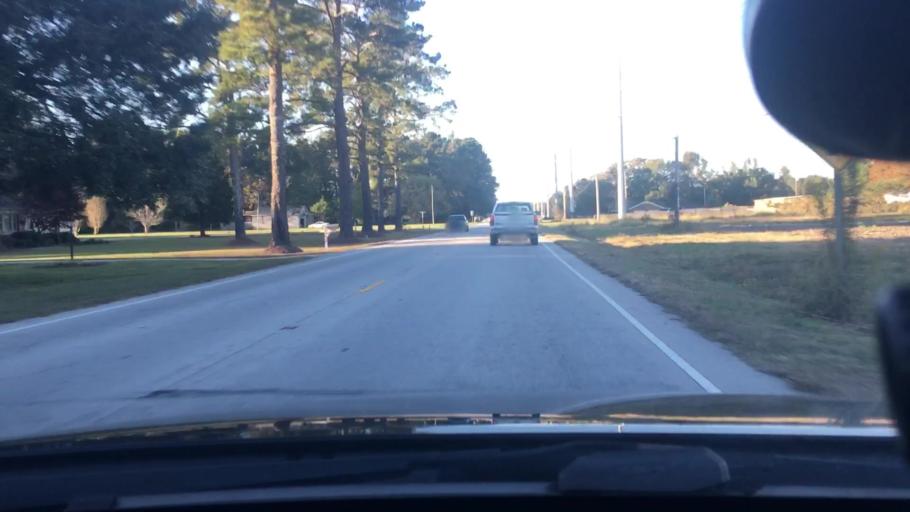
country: US
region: North Carolina
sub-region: Pitt County
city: Windsor
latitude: 35.5385
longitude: -77.3218
